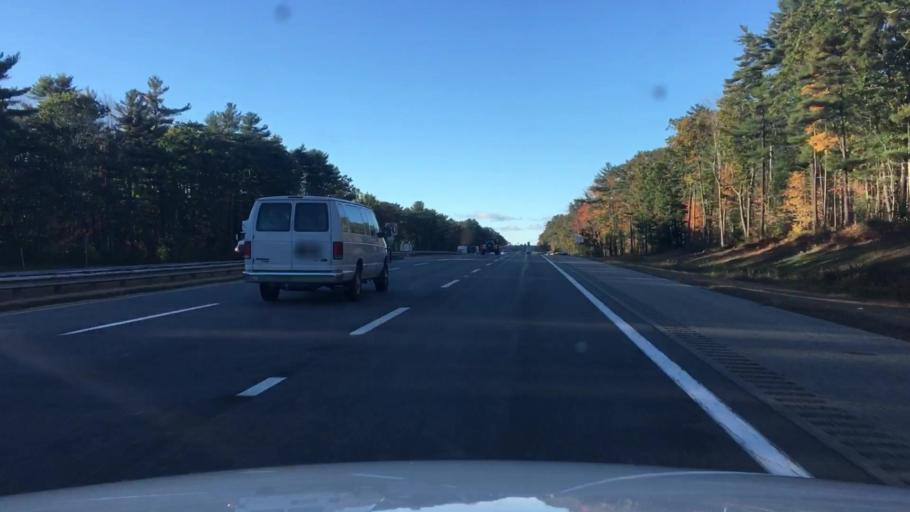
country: US
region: Maine
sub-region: York County
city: West Kennebunk
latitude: 43.3750
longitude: -70.5795
